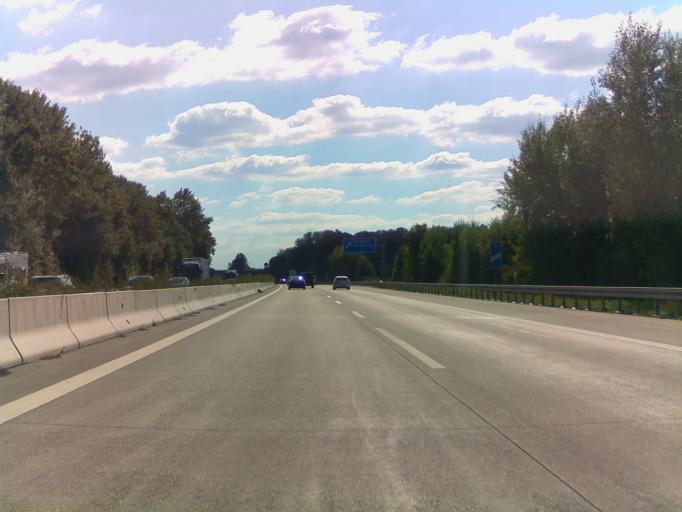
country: DE
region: Baden-Wuerttemberg
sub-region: Karlsruhe Region
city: Hemsbach
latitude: 49.5989
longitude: 8.6310
